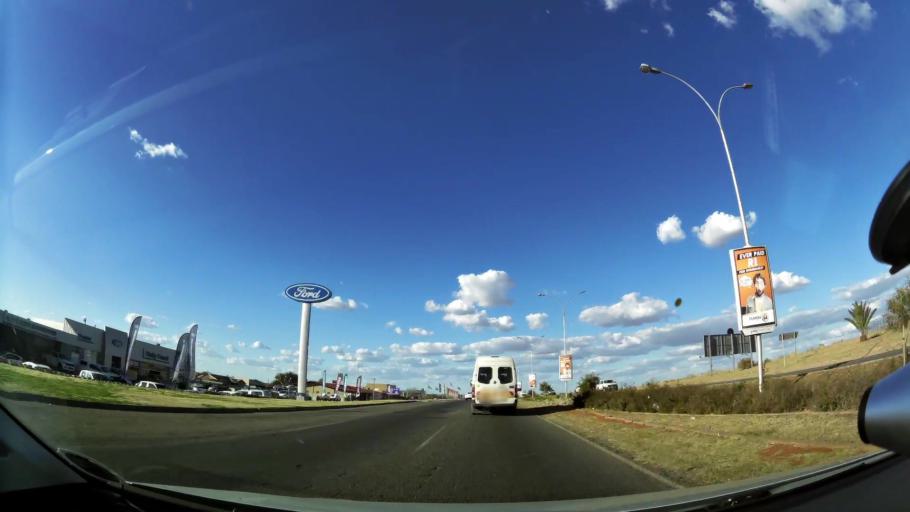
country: ZA
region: North-West
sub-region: Dr Kenneth Kaunda District Municipality
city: Klerksdorp
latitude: -26.8523
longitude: 26.6865
